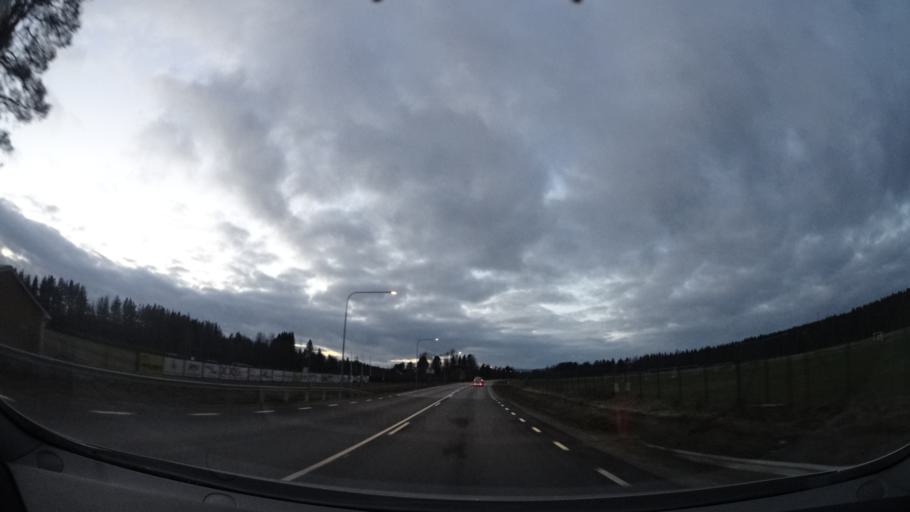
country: SE
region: Vaesterbotten
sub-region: Asele Kommun
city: Asele
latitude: 64.1613
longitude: 17.3342
